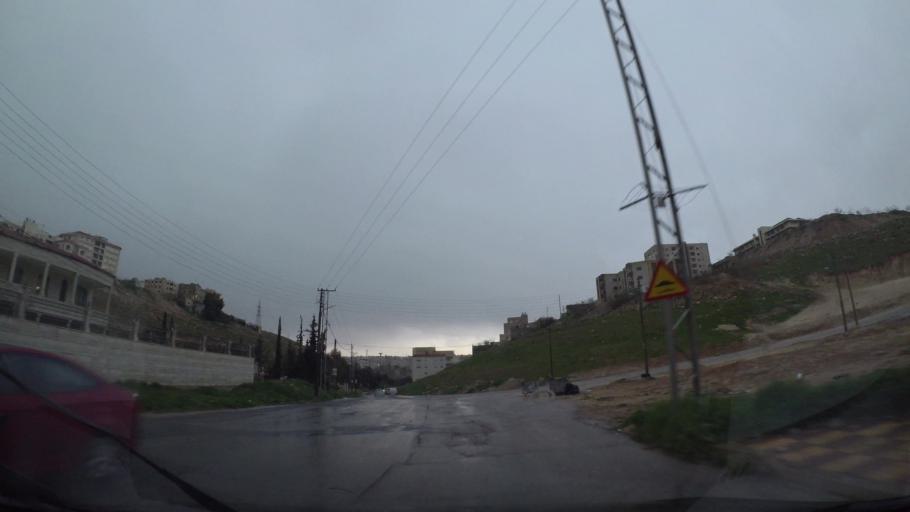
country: JO
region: Amman
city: Amman
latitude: 31.9935
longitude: 35.9714
